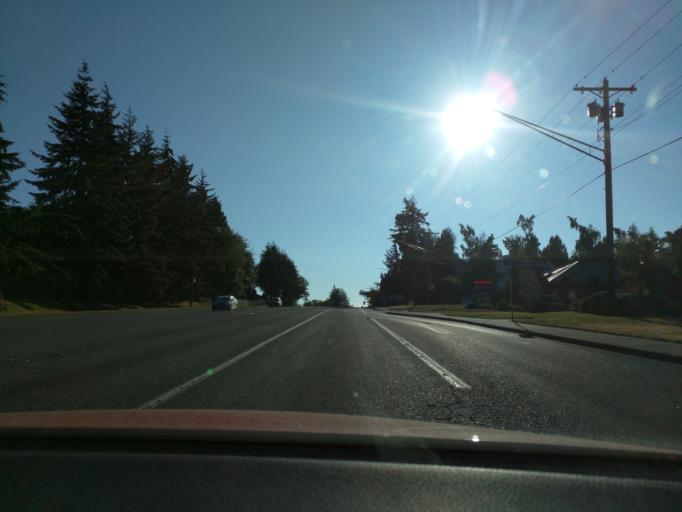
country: US
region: Washington
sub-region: Snohomish County
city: Martha Lake
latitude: 47.8819
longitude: -122.2453
